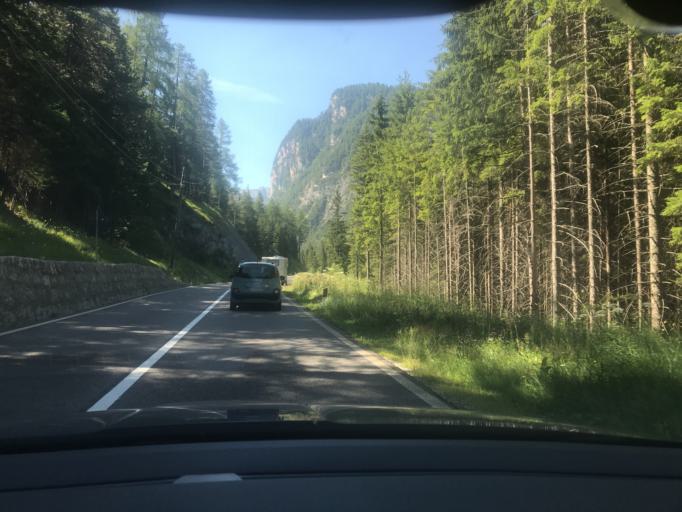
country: IT
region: Trentino-Alto Adige
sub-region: Bolzano
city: Dobbiaco
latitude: 46.7003
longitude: 12.2229
